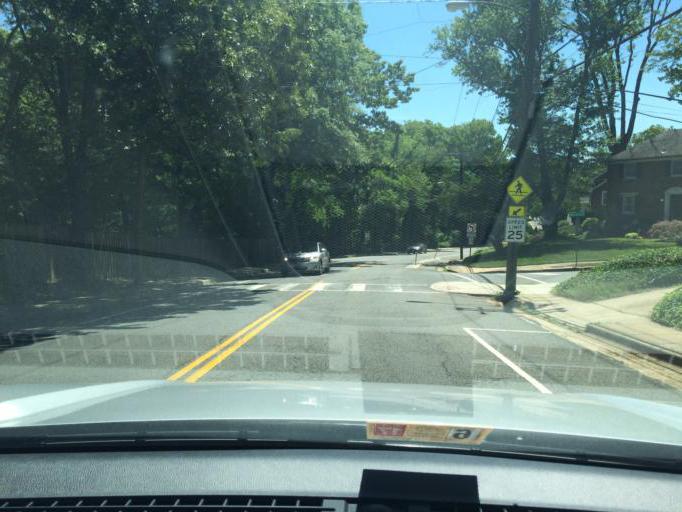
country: US
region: Virginia
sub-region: Fairfax County
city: Huntington
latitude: 38.8261
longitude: -77.0792
